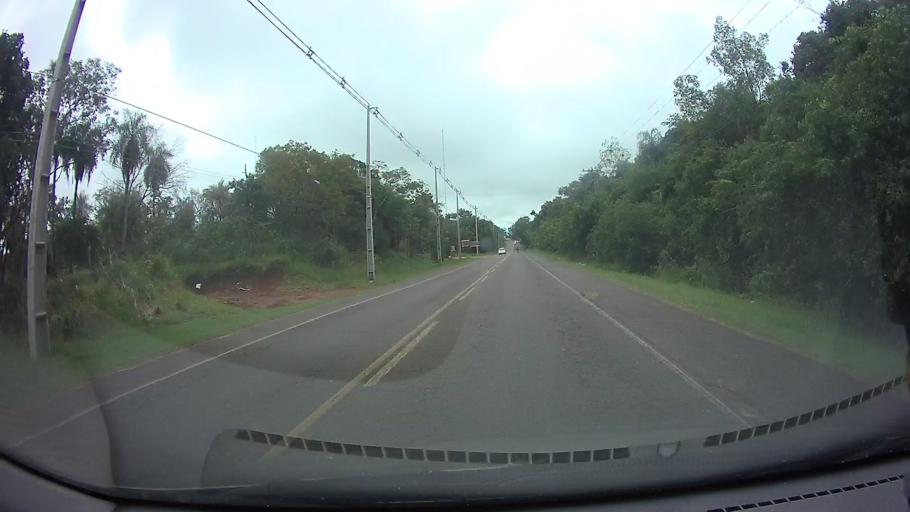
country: PY
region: Cordillera
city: Altos
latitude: -25.2796
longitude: -57.2615
